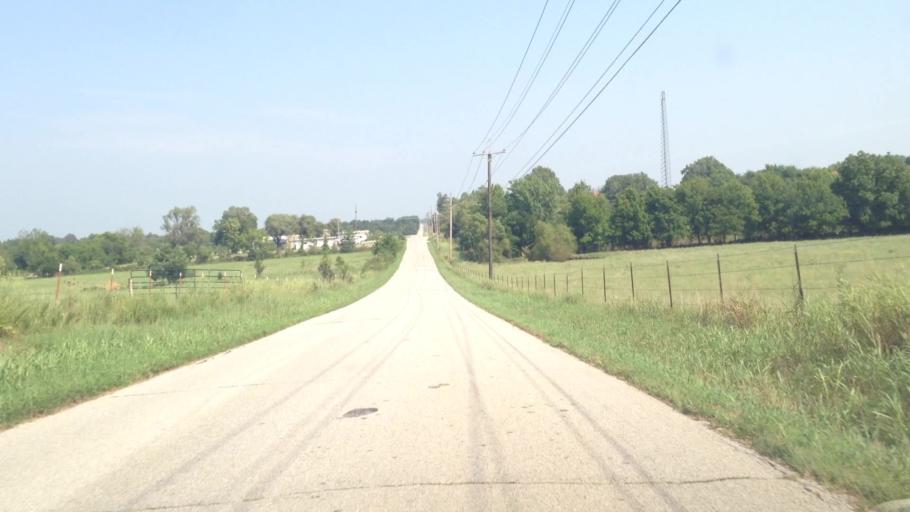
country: US
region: Oklahoma
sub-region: Craig County
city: Vinita
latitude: 36.6525
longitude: -95.1256
